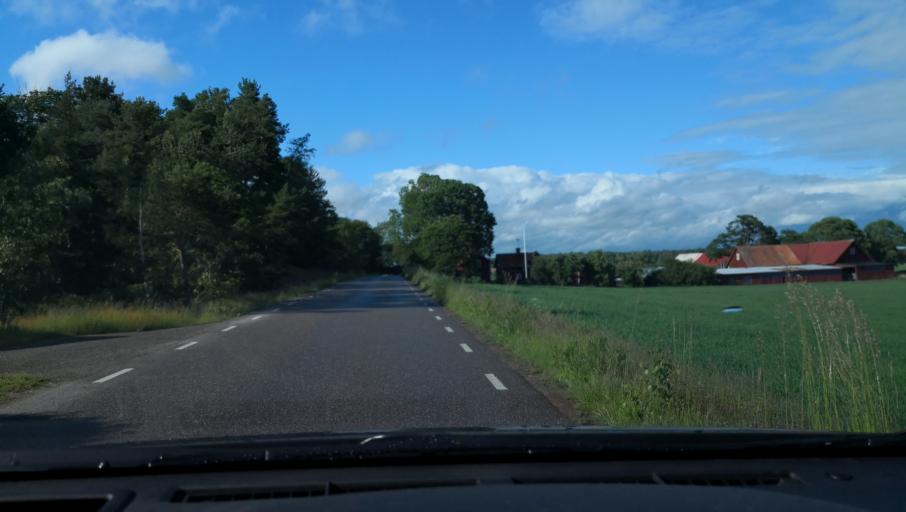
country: SE
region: OErebro
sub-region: Lindesbergs Kommun
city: Fellingsbro
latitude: 59.3154
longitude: 15.6788
